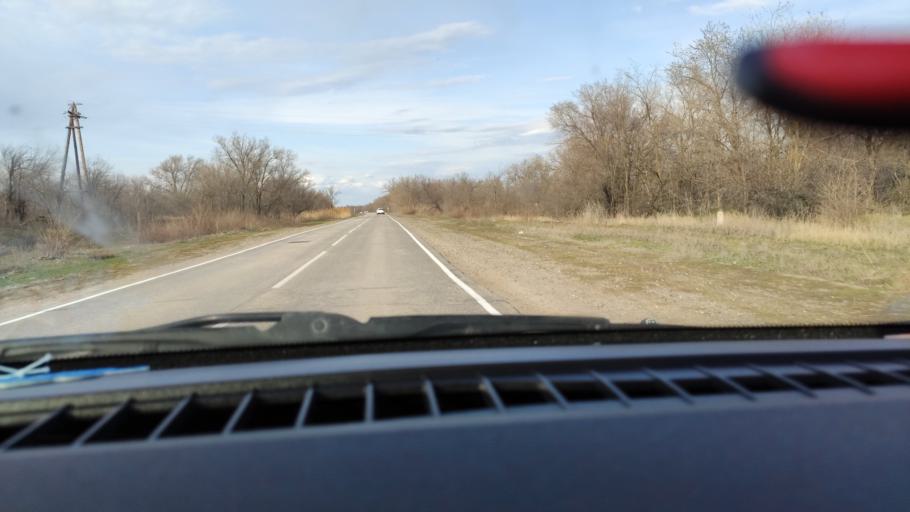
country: RU
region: Saratov
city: Privolzhskiy
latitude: 51.2417
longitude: 45.9308
